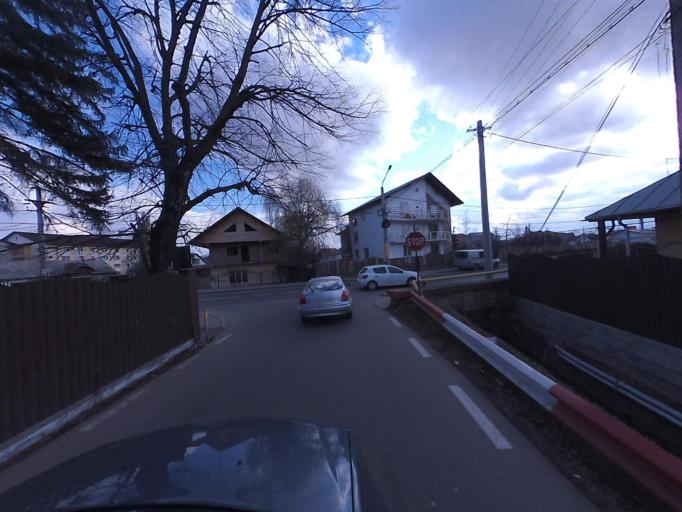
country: RO
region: Neamt
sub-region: Oras Targu Neamt
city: Targu Neamt
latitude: 47.2066
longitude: 26.3744
